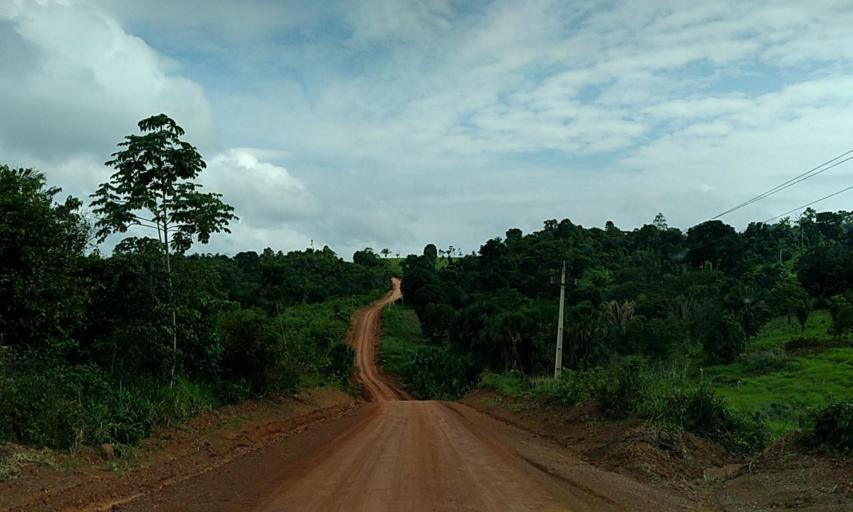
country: BR
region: Para
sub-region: Senador Jose Porfirio
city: Senador Jose Porfirio
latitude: -3.0733
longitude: -51.6350
